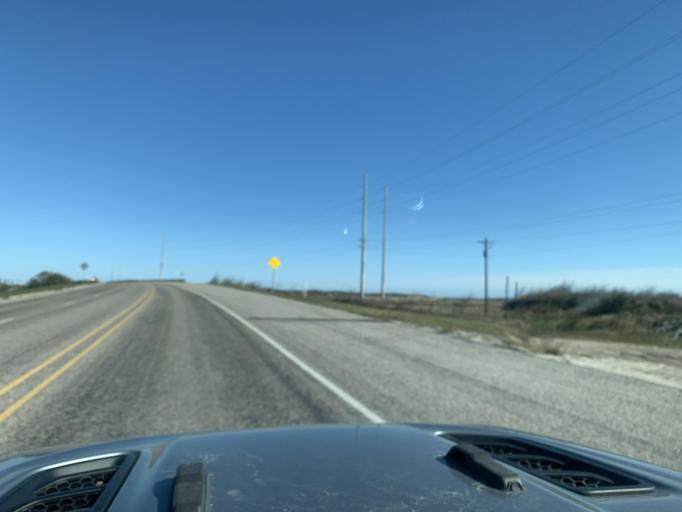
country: US
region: Texas
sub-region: Nueces County
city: Corpus Christi
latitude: 27.6181
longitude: -97.2169
